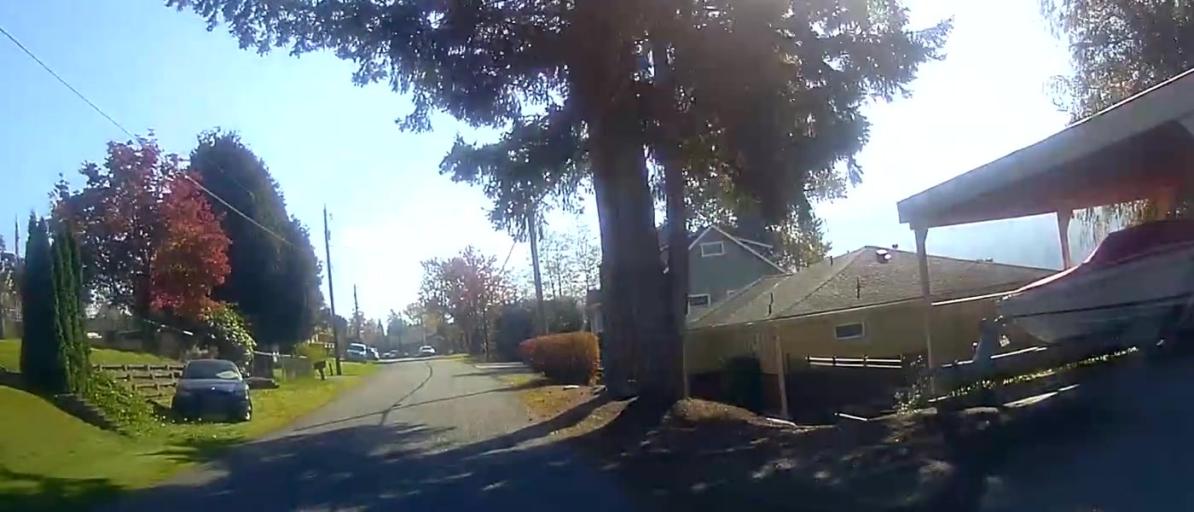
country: US
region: Washington
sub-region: Skagit County
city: Big Lake
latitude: 48.3972
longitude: -122.2396
